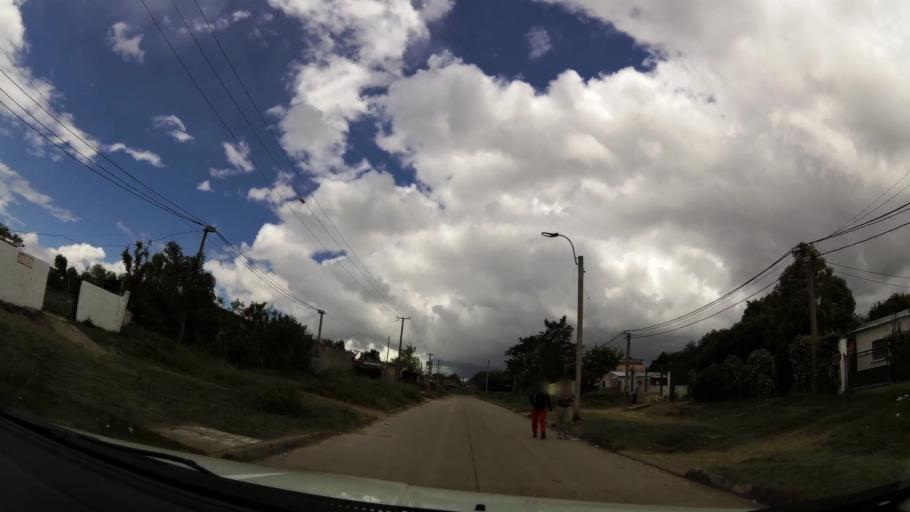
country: UY
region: Montevideo
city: Montevideo
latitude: -34.8257
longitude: -56.1656
